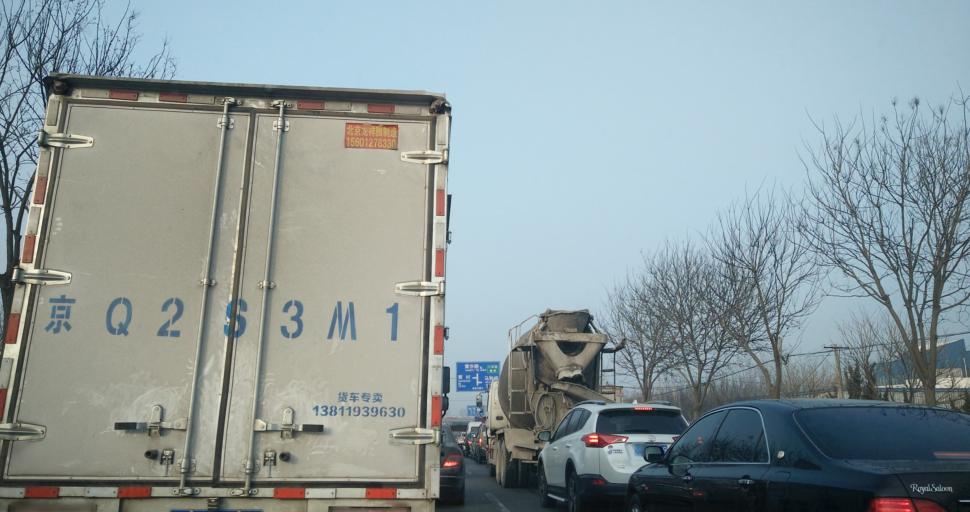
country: CN
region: Beijing
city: Yinghai
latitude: 39.7169
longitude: 116.4028
